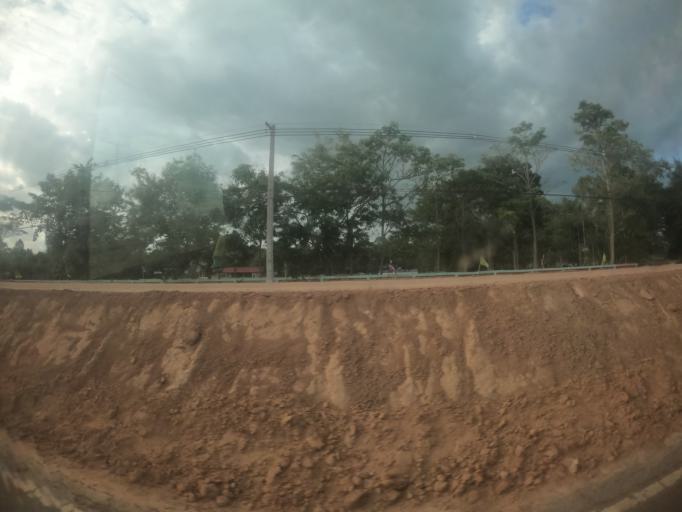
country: TH
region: Surin
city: Kap Choeng
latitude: 14.4656
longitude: 103.6382
